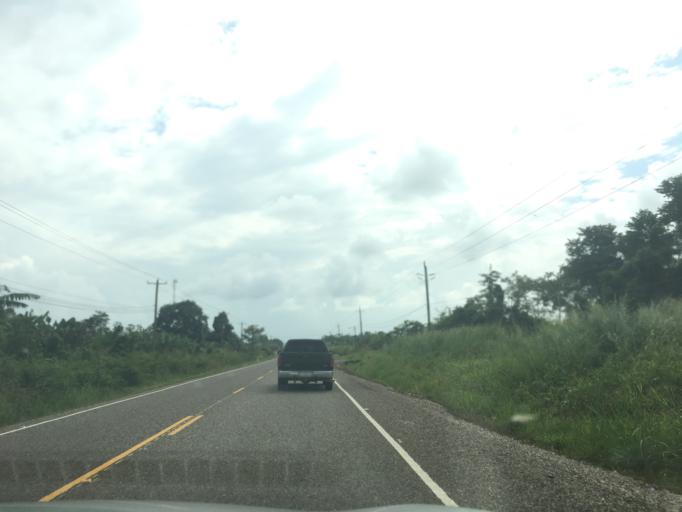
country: BZ
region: Stann Creek
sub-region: Dangriga
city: Dangriga
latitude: 16.9956
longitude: -88.3013
